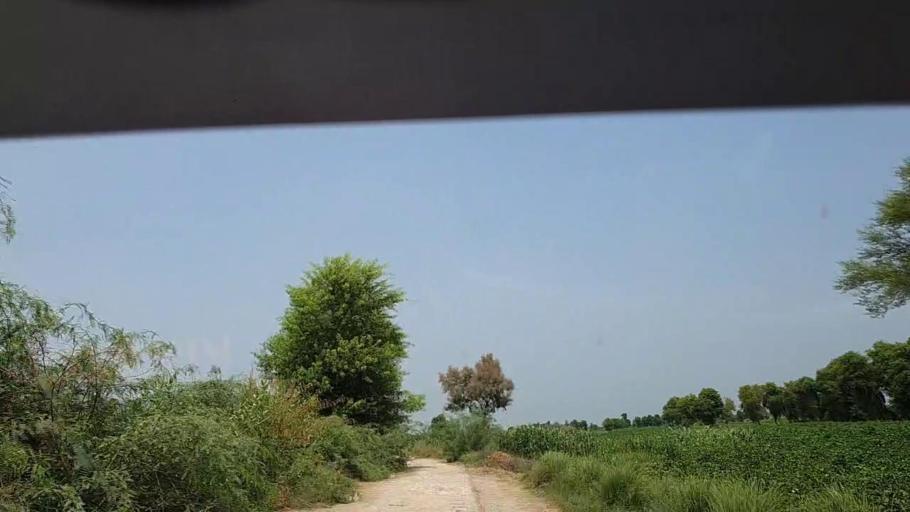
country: PK
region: Sindh
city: Adilpur
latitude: 27.8837
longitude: 69.2590
